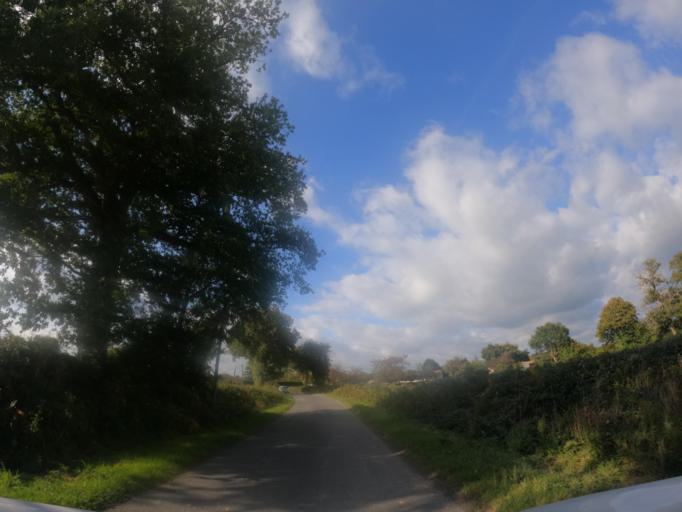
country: FR
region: Poitou-Charentes
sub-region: Departement des Deux-Sevres
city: La Foret-sur-Sevre
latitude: 46.7806
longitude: -0.6153
